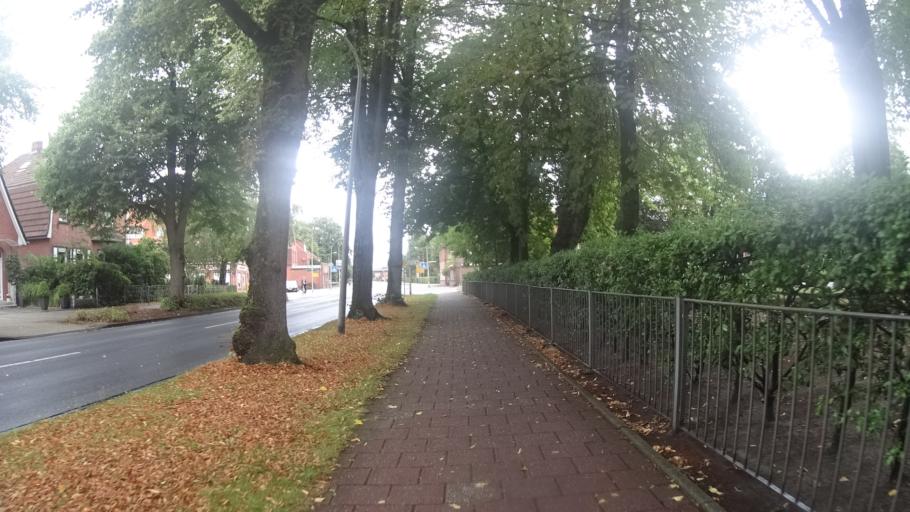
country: DE
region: Lower Saxony
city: Leer
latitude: 53.2371
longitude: 7.4552
